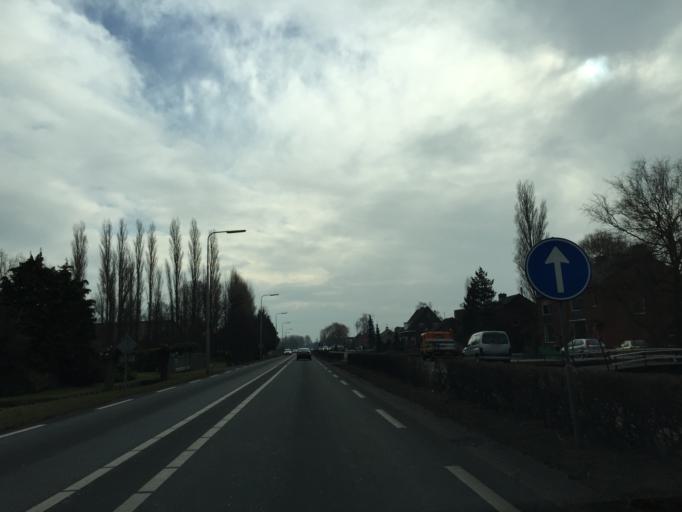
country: NL
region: South Holland
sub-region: Gemeente Capelle aan den IJssel
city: Capelle aan den IJssel
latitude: 51.9871
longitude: 4.6036
